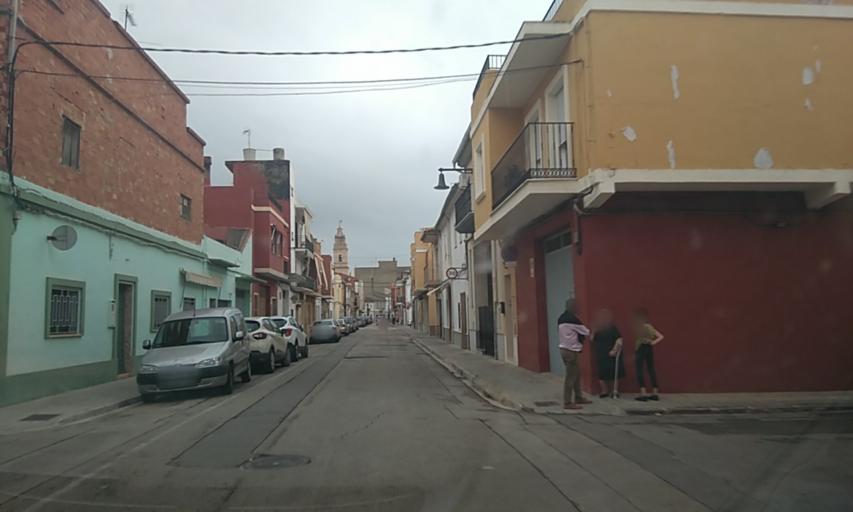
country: ES
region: Valencia
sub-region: Provincia de Valencia
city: L'Alcudia
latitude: 39.1986
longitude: -0.5091
